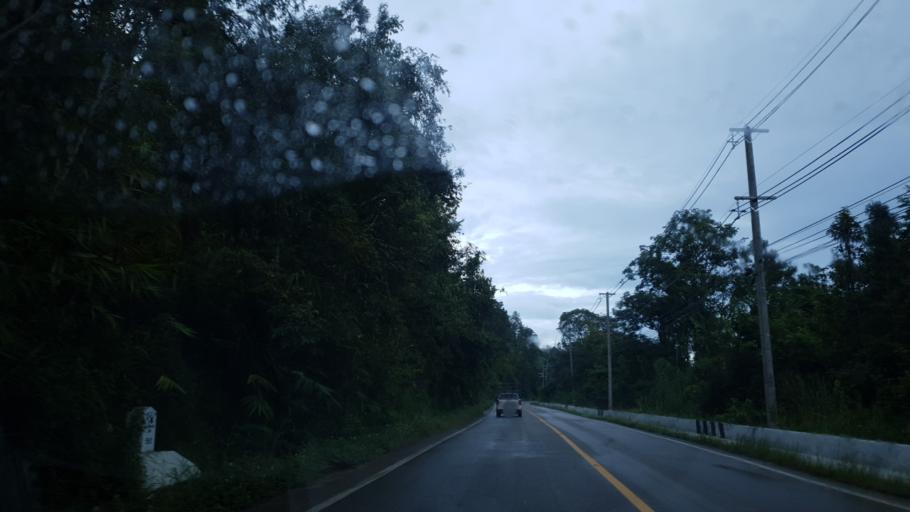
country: TH
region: Mae Hong Son
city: Ban Huai I Huak
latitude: 18.1492
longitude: 98.2063
